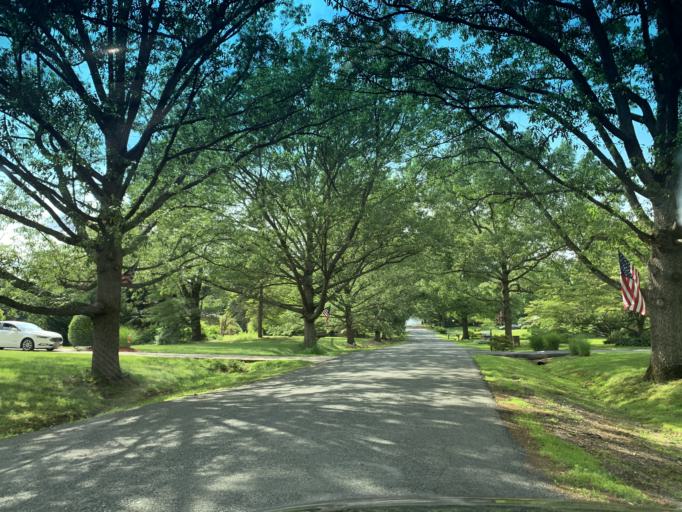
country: US
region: Maryland
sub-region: Harford County
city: Jarrettsville
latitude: 39.5996
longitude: -76.4607
